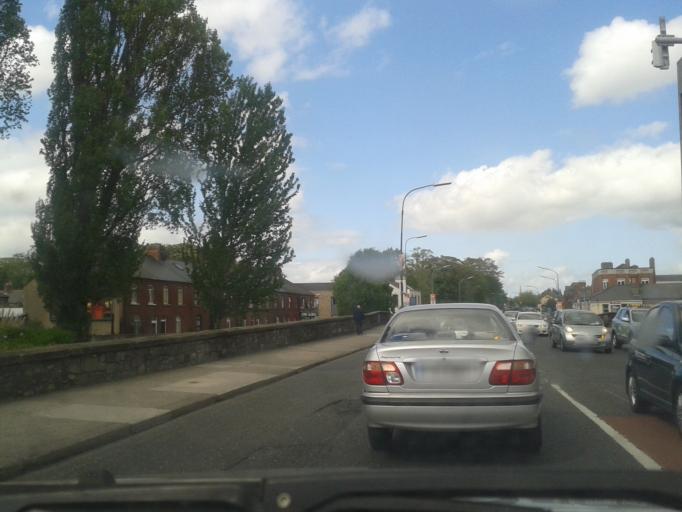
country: IE
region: Leinster
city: Drumcondra
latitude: 53.3678
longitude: -6.2555
